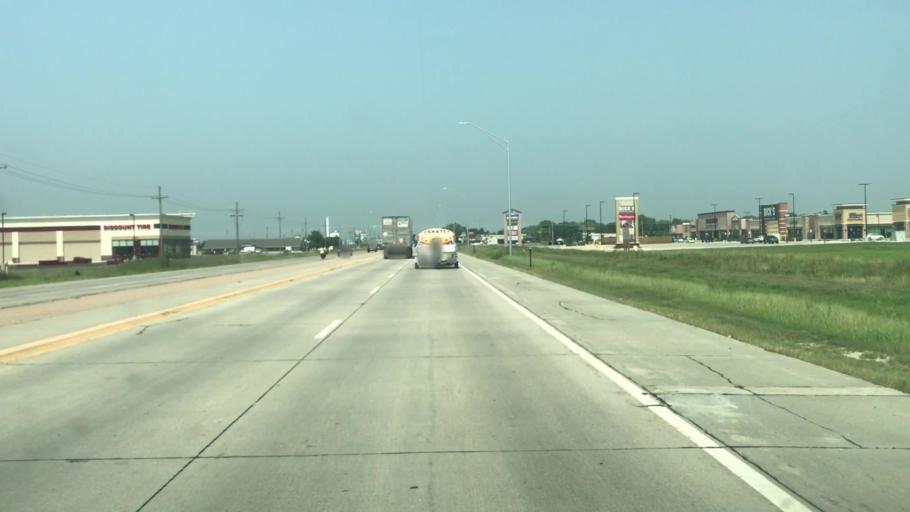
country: US
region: Nebraska
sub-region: Hall County
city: Grand Island
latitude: 40.9413
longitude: -98.3834
